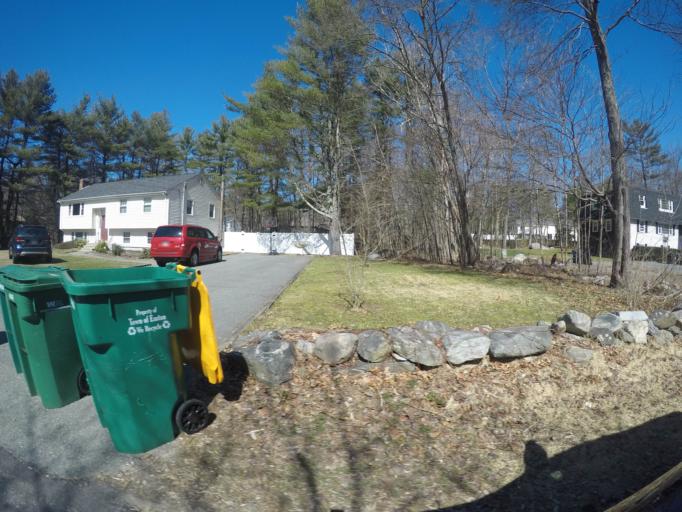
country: US
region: Massachusetts
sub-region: Bristol County
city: Easton
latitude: 42.0089
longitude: -71.1476
